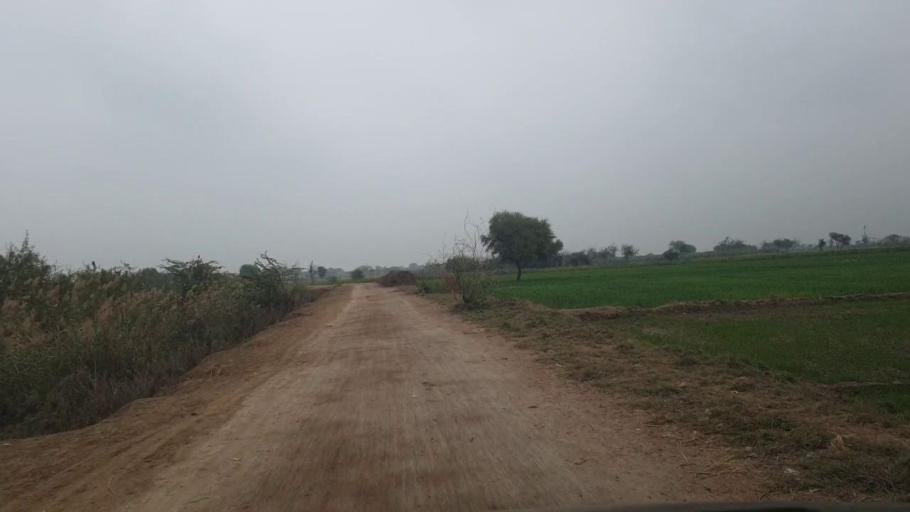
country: PK
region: Sindh
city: Tando Adam
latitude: 25.8418
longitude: 68.7117
